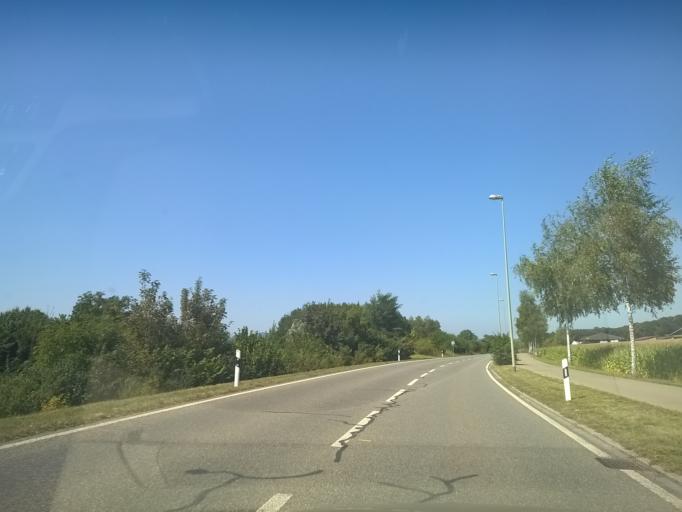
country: CH
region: Zurich
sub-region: Bezirk Buelach
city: Kloten / Freienberg (Chanzler-Chlini Chaseren)
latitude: 47.4627
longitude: 8.5753
